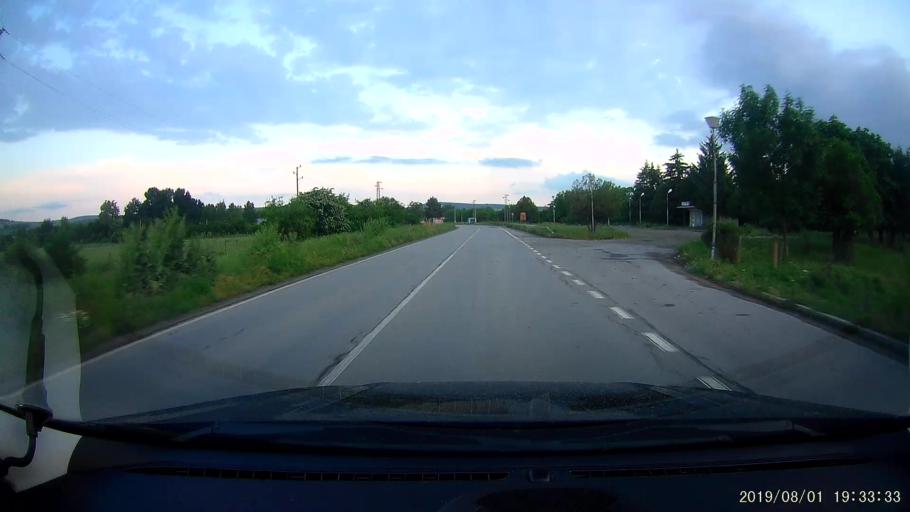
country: BG
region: Burgas
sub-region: Obshtina Sungurlare
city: Sungurlare
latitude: 42.7781
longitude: 26.8769
